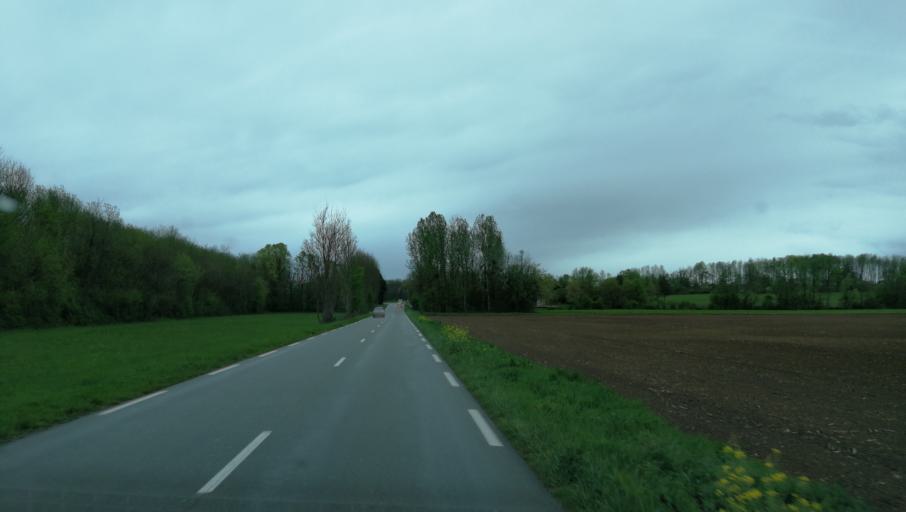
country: FR
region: Franche-Comte
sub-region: Departement du Jura
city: Bletterans
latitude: 46.7209
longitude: 5.4735
